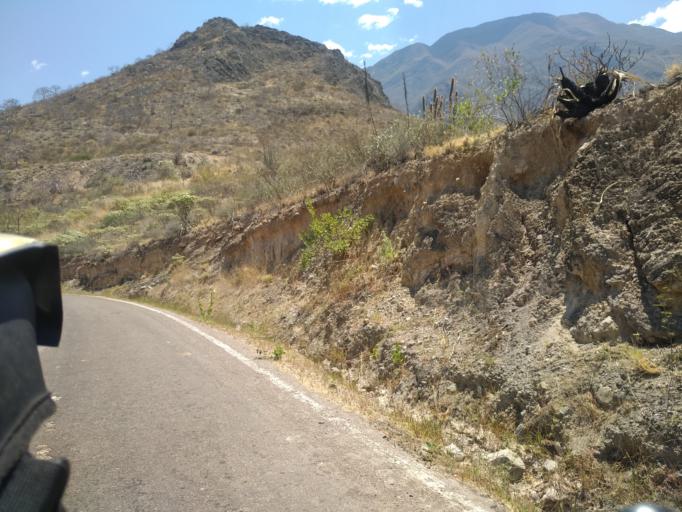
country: PE
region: Amazonas
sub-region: Provincia de Chachapoyas
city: Balsas
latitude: -6.8466
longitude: -78.0427
